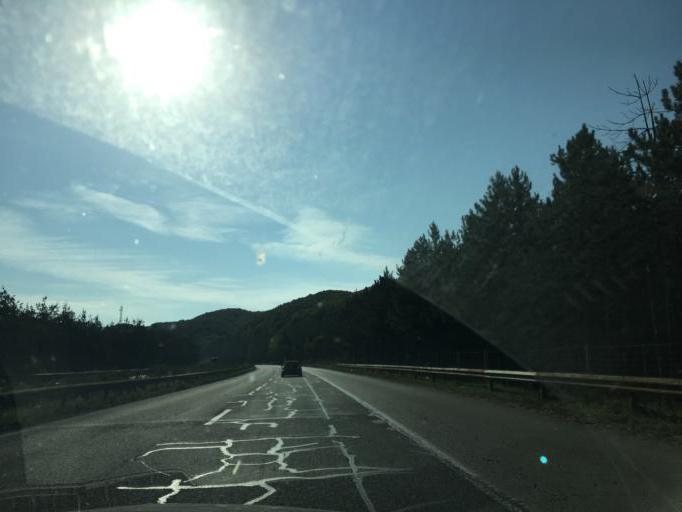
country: BG
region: Sofiya
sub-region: Obshtina Ikhtiman
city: Ikhtiman
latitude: 42.3586
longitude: 23.9071
